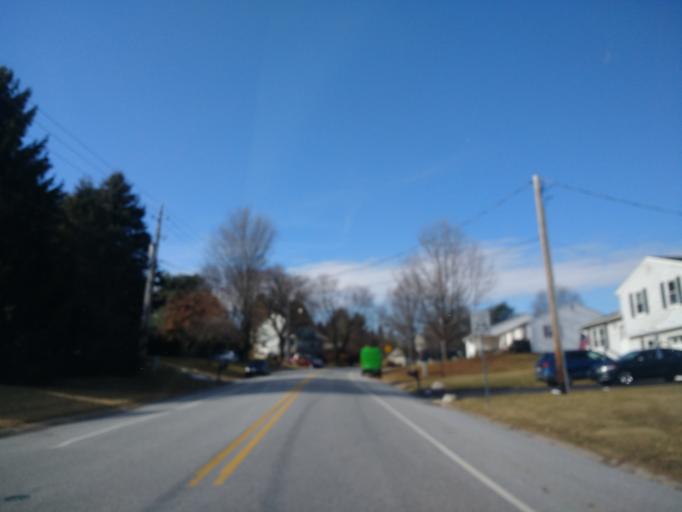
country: US
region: Pennsylvania
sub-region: York County
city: Spry
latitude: 39.9022
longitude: -76.6675
